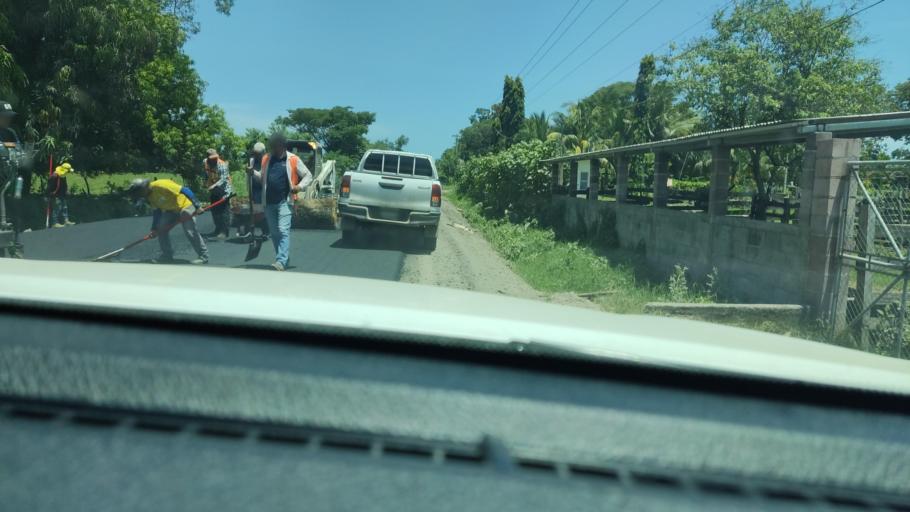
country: SV
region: Ahuachapan
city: San Francisco Menendez
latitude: 13.8410
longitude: -90.1206
